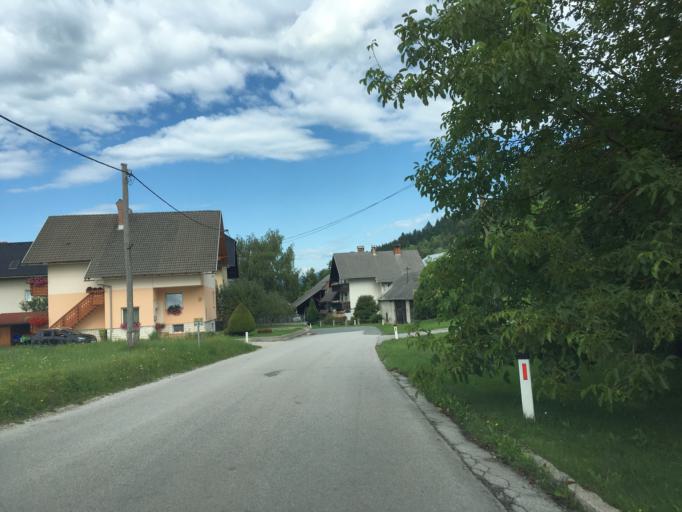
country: SI
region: Radovljica
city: Radovljica
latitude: 46.3748
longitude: 14.1941
